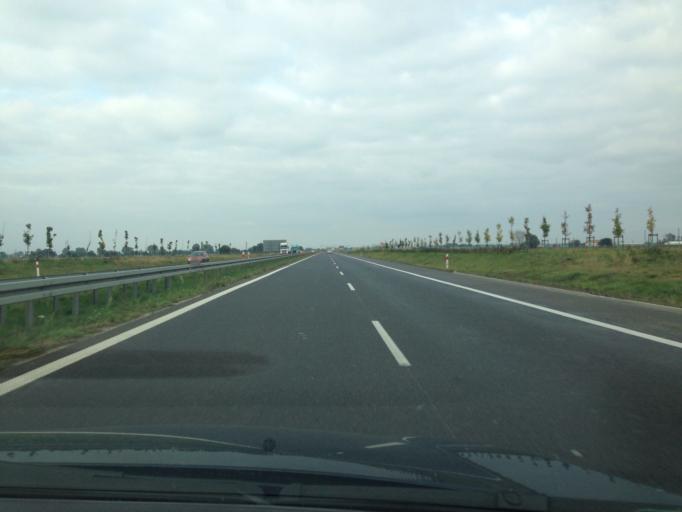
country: PL
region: Greater Poland Voivodeship
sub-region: Powiat poznanski
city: Kleszczewo
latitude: 52.3292
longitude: 17.1472
